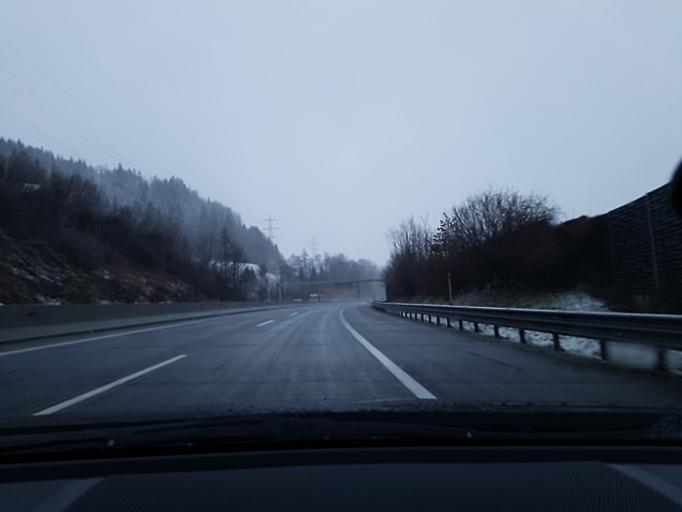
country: AT
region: Salzburg
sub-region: Politischer Bezirk Hallein
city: Kuchl
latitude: 47.6152
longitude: 13.1391
